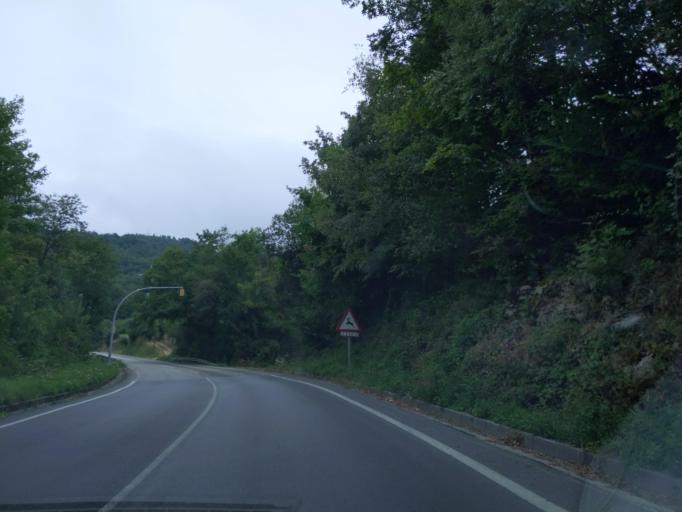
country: ES
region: Asturias
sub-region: Province of Asturias
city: Pola de Laviana
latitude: 43.2247
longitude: -5.4588
